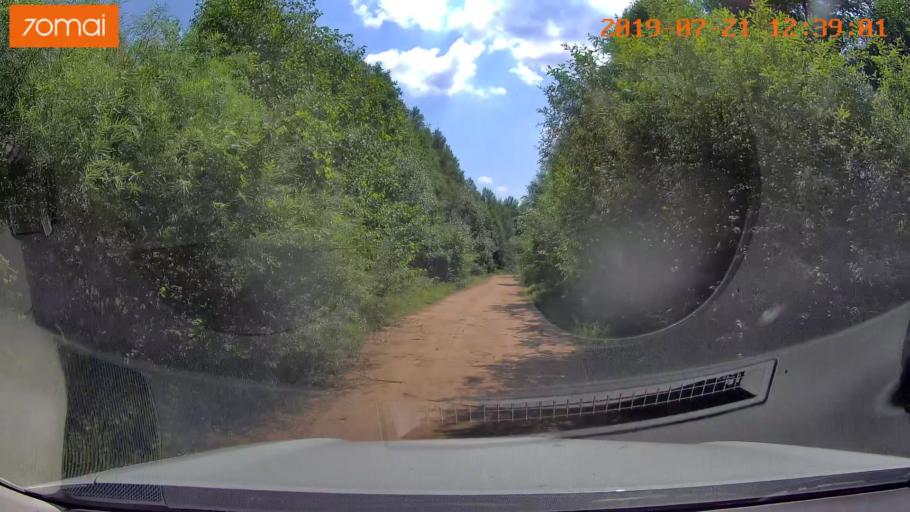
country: BY
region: Grodnenskaya
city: Lyubcha
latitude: 53.8576
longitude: 26.0153
